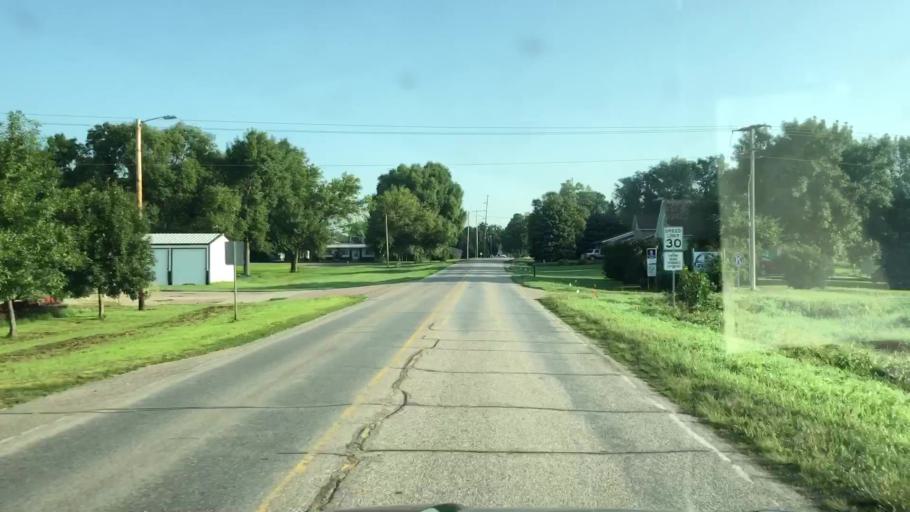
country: US
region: Iowa
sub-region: Lyon County
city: George
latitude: 43.3379
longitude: -95.9986
